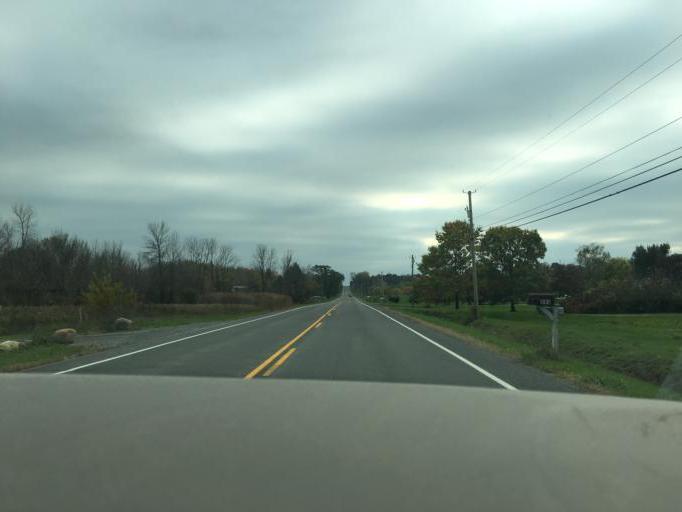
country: US
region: New York
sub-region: Wayne County
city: Macedon
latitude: 43.0104
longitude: -77.3244
